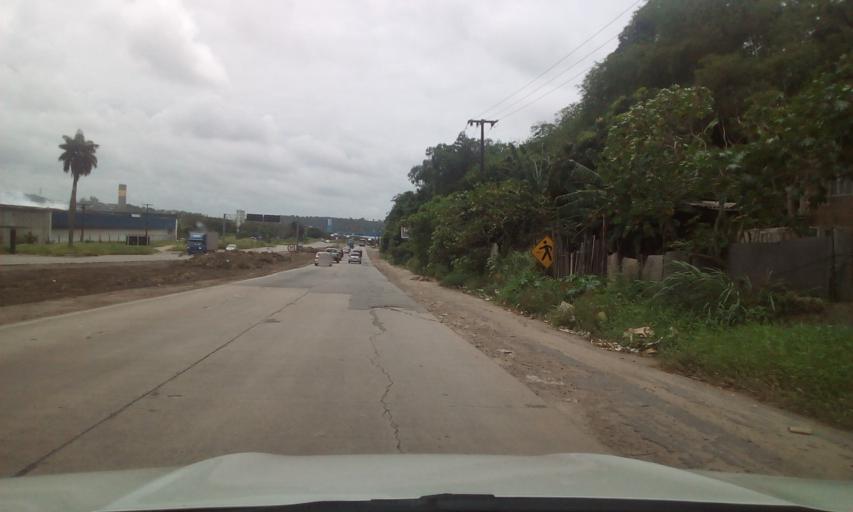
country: BR
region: Pernambuco
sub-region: Abreu E Lima
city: Abreu e Lima
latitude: -7.9273
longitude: -34.8976
